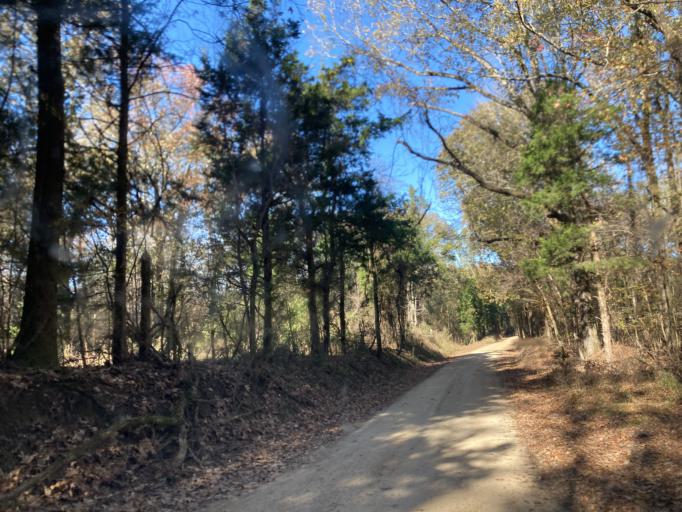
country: US
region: Mississippi
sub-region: Yazoo County
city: Yazoo City
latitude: 32.6975
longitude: -90.4936
